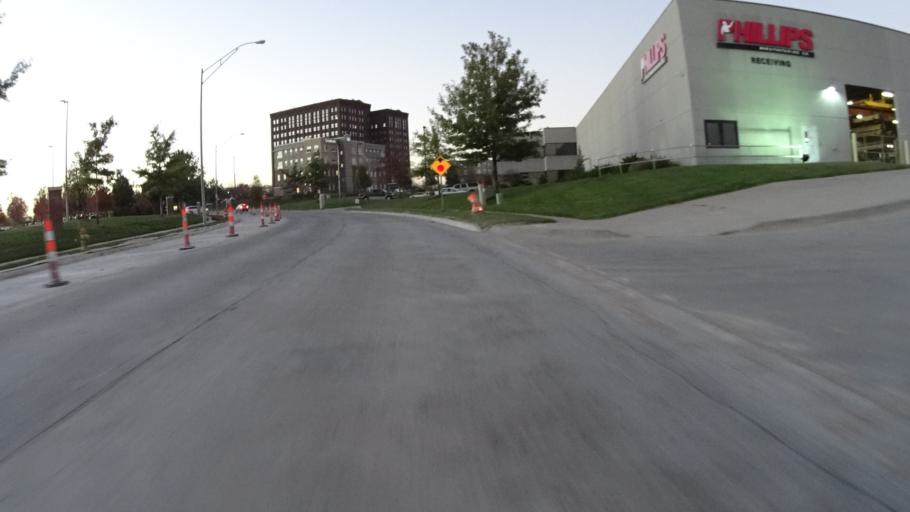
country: US
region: Nebraska
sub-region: Douglas County
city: Omaha
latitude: 41.2080
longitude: -95.9541
